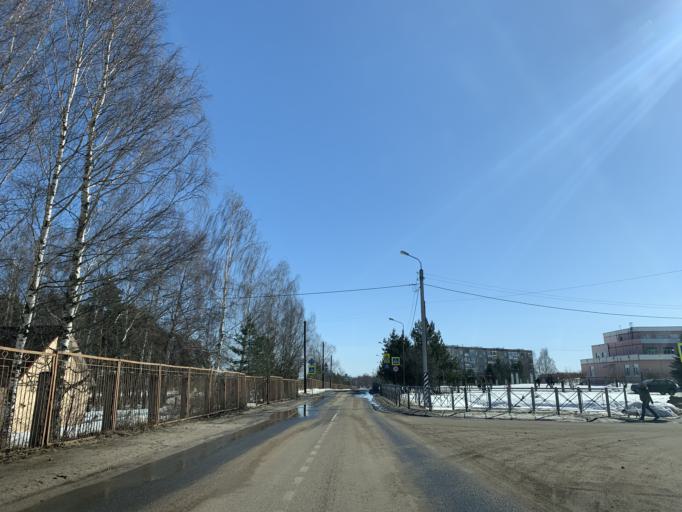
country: RU
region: Jaroslavl
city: Konstantinovskiy
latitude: 57.8403
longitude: 39.5801
